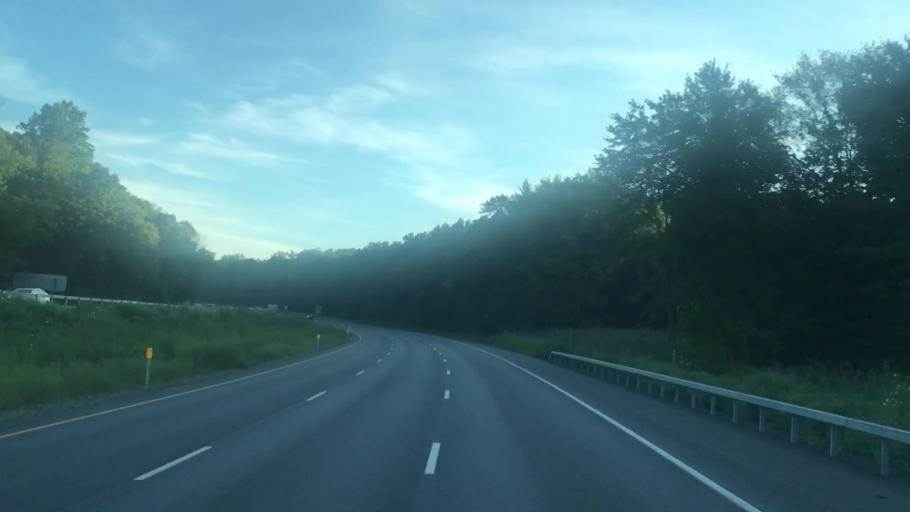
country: US
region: New York
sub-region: Putnam County
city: Brewster
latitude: 41.3766
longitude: -73.6043
